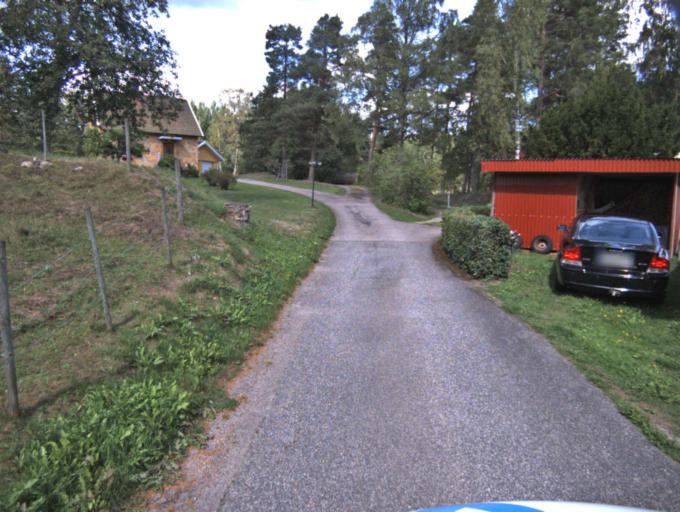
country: SE
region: Vaestra Goetaland
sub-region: Ulricehamns Kommun
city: Ulricehamn
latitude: 57.9367
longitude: 13.5023
